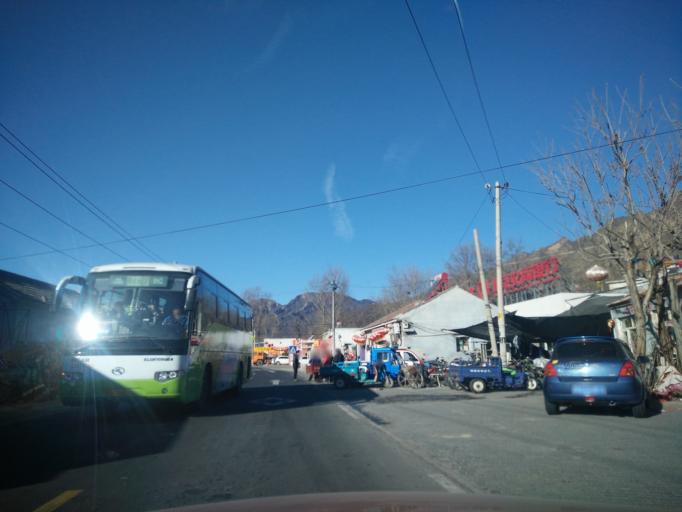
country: CN
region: Beijing
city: Yanchi
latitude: 40.0162
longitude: 115.8267
